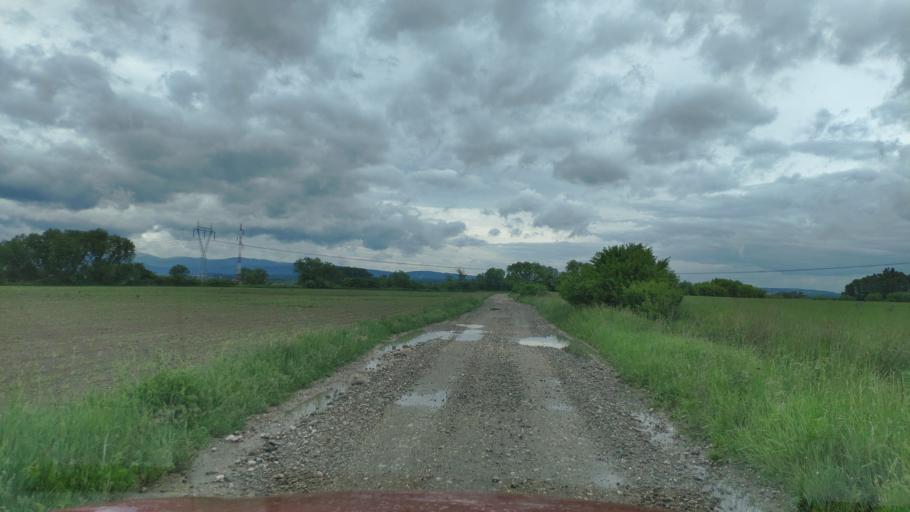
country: SK
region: Kosicky
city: Moldava nad Bodvou
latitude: 48.5593
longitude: 21.1160
